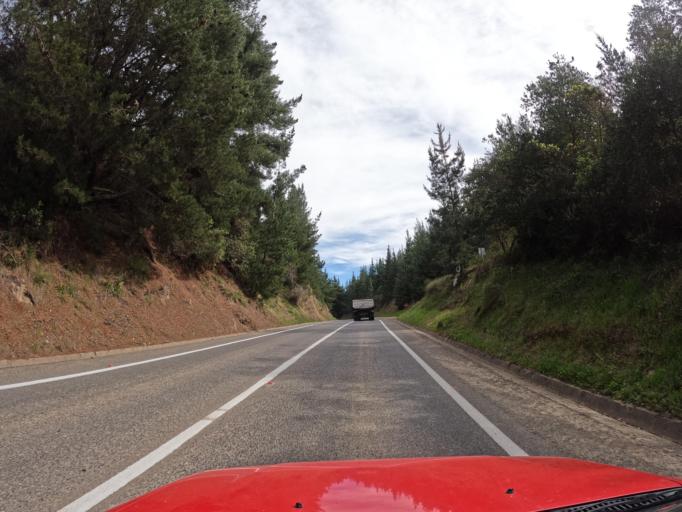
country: CL
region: Maule
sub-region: Provincia de Talca
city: Talca
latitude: -35.2913
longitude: -71.9757
